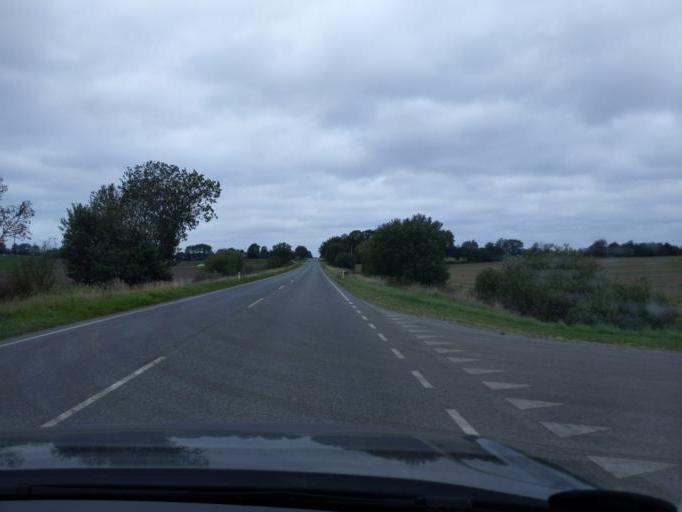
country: DK
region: Central Jutland
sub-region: Randers Kommune
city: Spentrup
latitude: 56.5311
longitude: 9.9148
